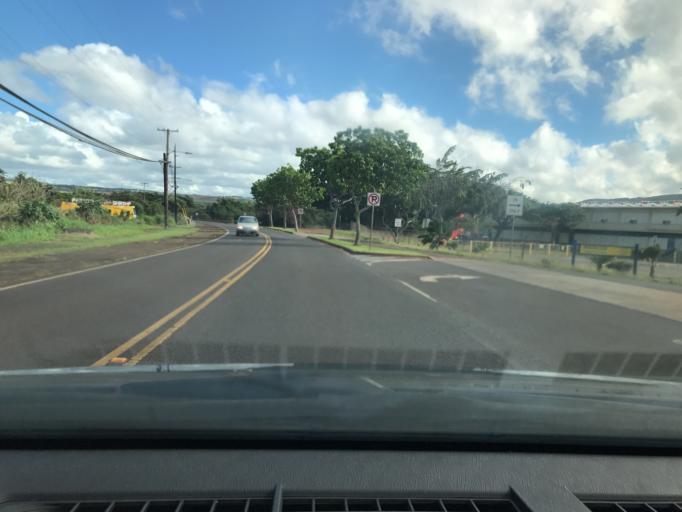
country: US
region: Hawaii
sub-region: Honolulu County
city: Waialua
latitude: 21.5765
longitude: -158.1216
